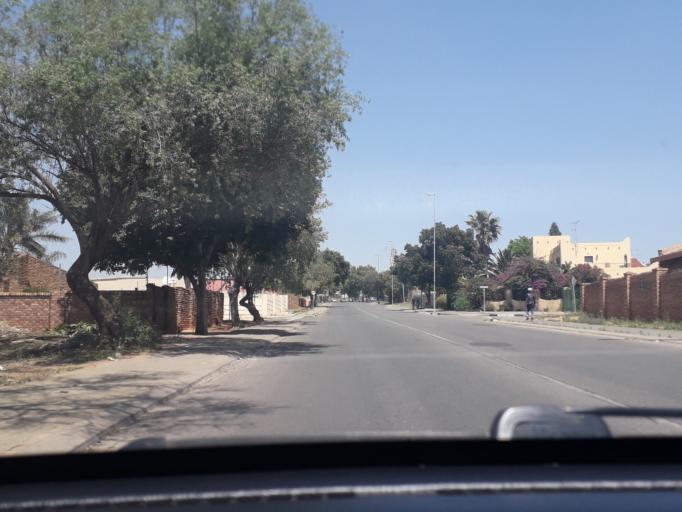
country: ZA
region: Gauteng
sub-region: City of Johannesburg Metropolitan Municipality
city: Modderfontein
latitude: -26.0933
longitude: 28.0946
